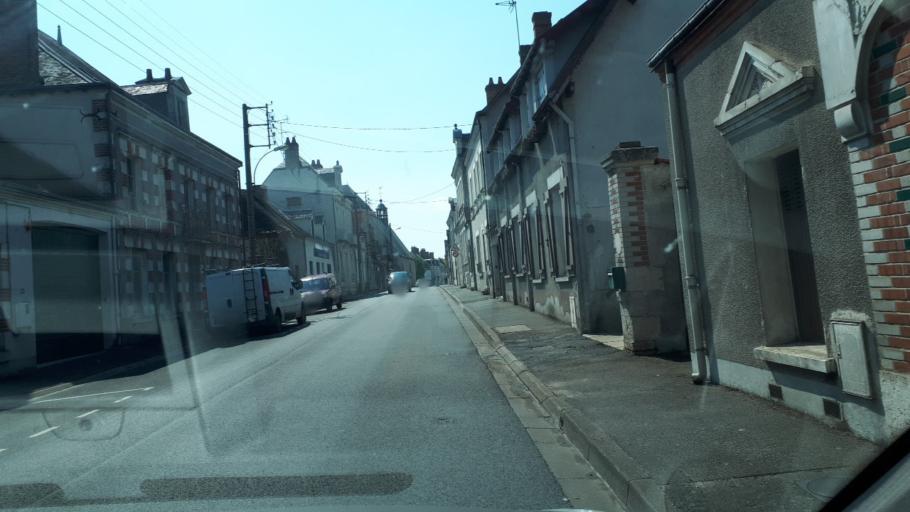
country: FR
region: Centre
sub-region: Departement du Loir-et-Cher
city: Romorantin-Lanthenay
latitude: 47.3644
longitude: 1.7417
